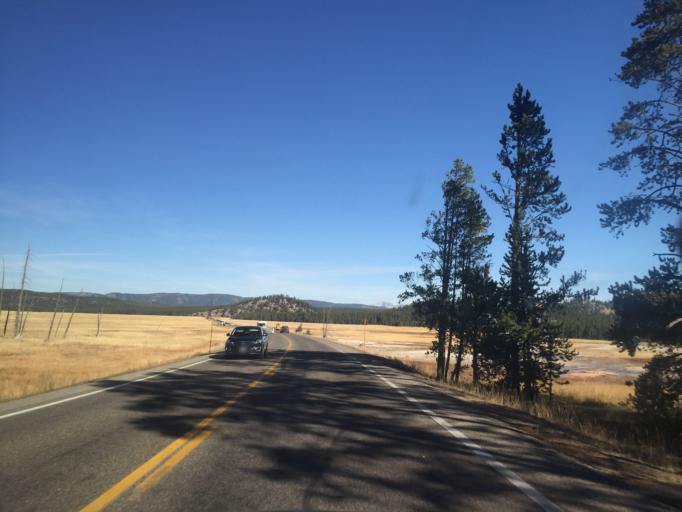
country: US
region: Montana
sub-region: Gallatin County
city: West Yellowstone
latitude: 44.5562
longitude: -110.8078
